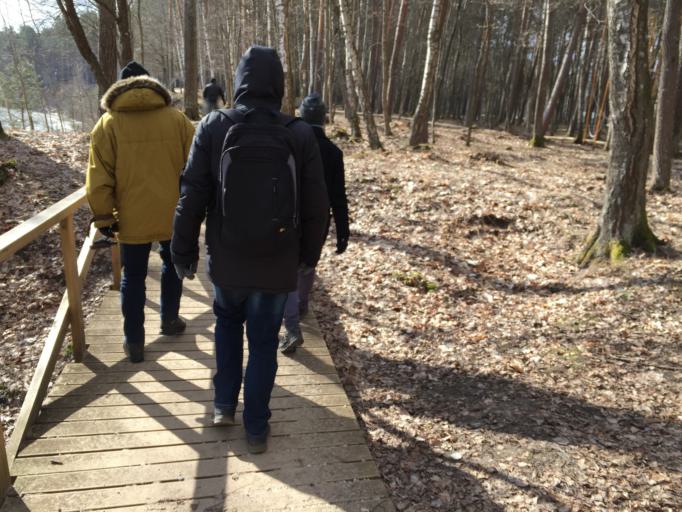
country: LV
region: Valmieras Rajons
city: Valmiera
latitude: 57.5415
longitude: 25.4450
